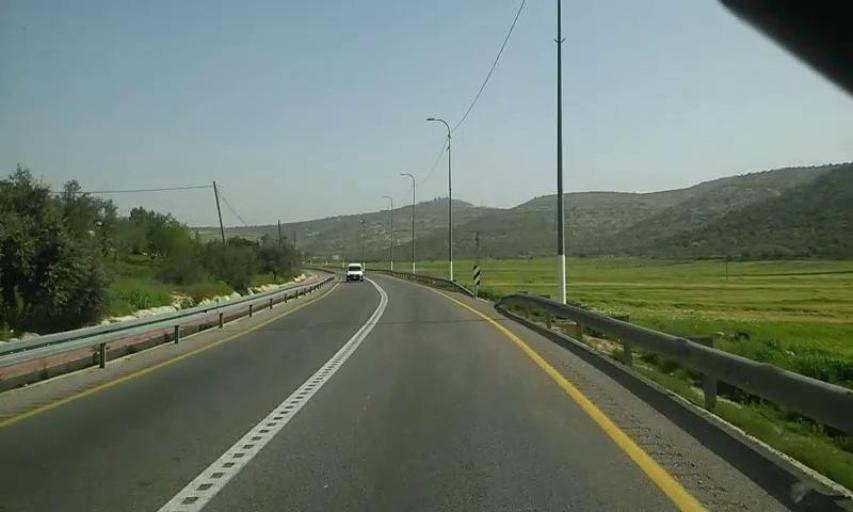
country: PS
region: West Bank
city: As Sawiyah
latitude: 32.0812
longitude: 35.2613
